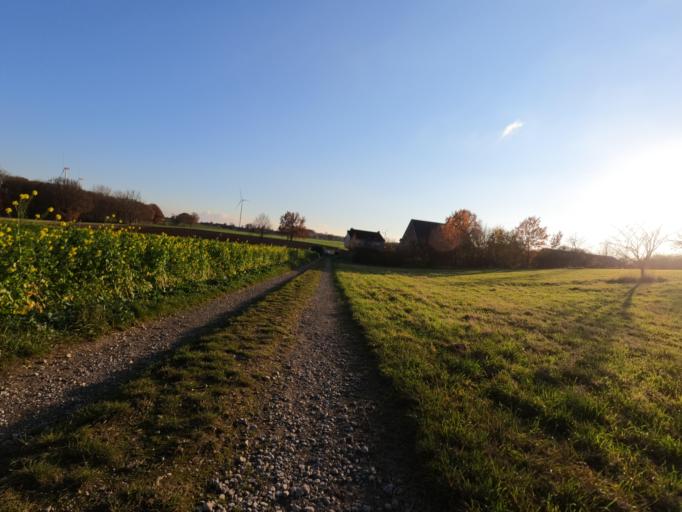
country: DE
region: North Rhine-Westphalia
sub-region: Regierungsbezirk Koln
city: Heinsberg
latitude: 51.0253
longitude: 6.1368
